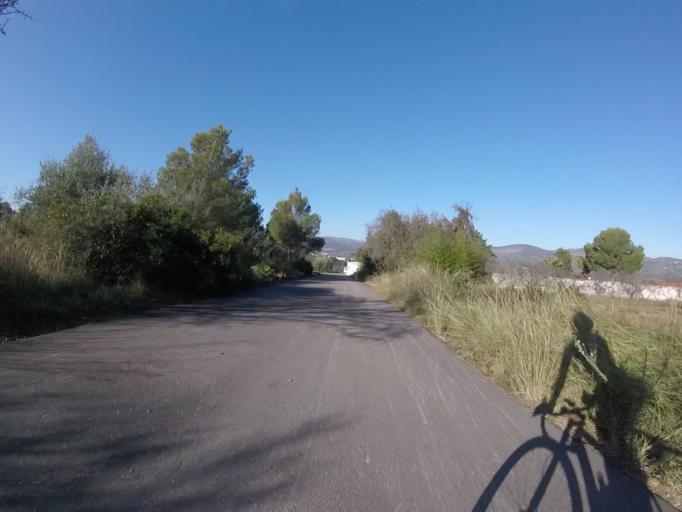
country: ES
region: Valencia
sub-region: Provincia de Castello
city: Santa Magdalena de Pulpis
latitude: 40.3548
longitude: 0.3109
